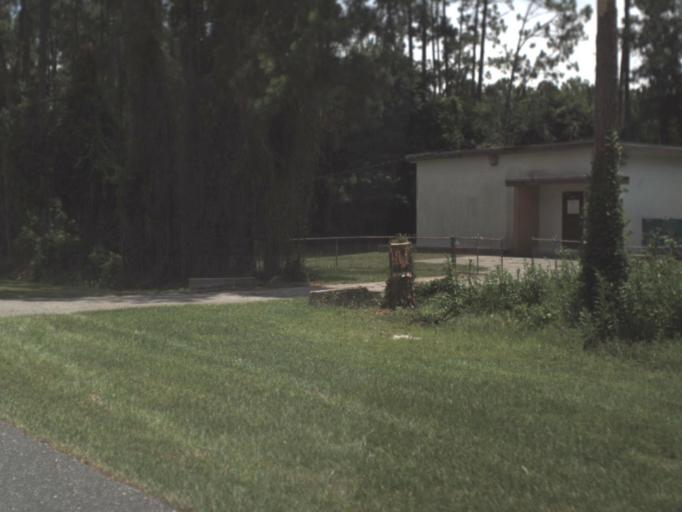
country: US
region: Florida
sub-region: Union County
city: Lake Butler
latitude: 30.0701
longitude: -82.2167
